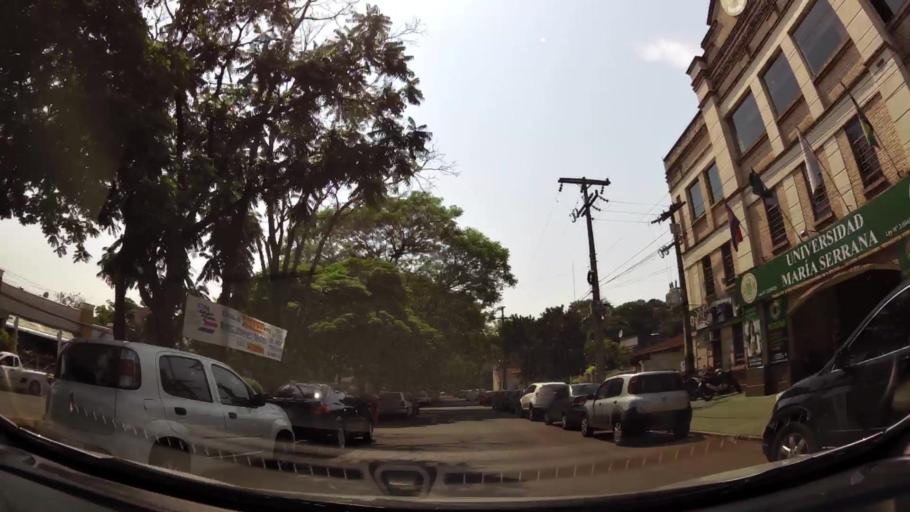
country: PY
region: Alto Parana
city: Presidente Franco
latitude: -25.5217
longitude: -54.6171
